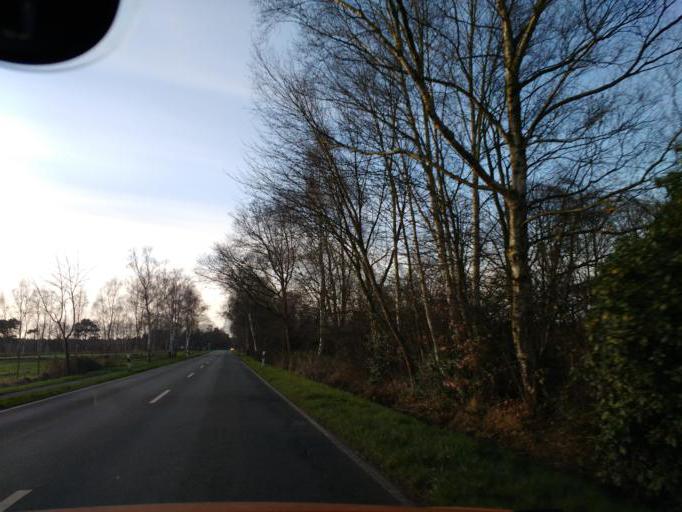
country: DE
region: Lower Saxony
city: Hude
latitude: 53.1023
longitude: 8.4262
